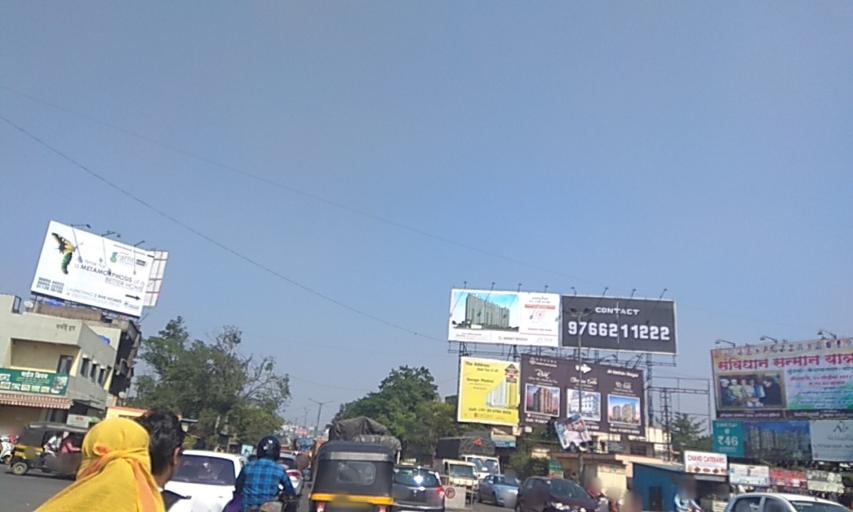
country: IN
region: Maharashtra
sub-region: Pune Division
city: Lohogaon
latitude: 18.5328
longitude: 73.9329
